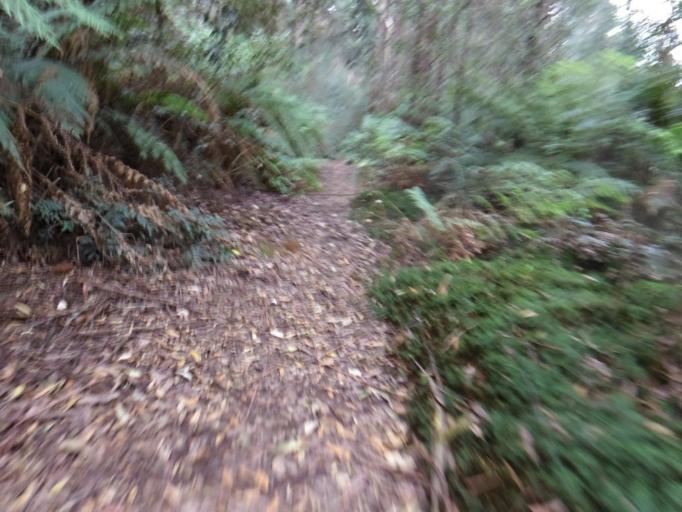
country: AU
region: Victoria
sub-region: Yarra Ranges
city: Healesville
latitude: -37.5209
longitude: 145.5212
